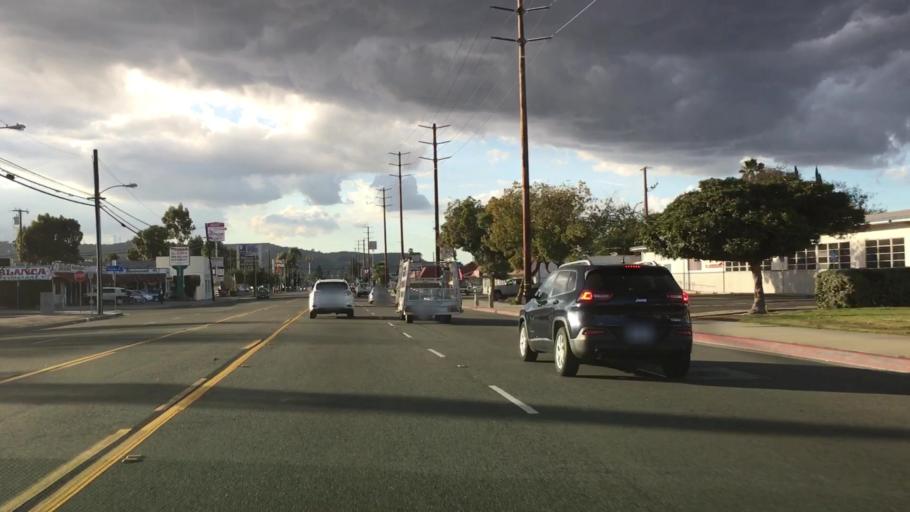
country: US
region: California
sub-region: Los Angeles County
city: La Puente
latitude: 34.0097
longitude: -117.9590
